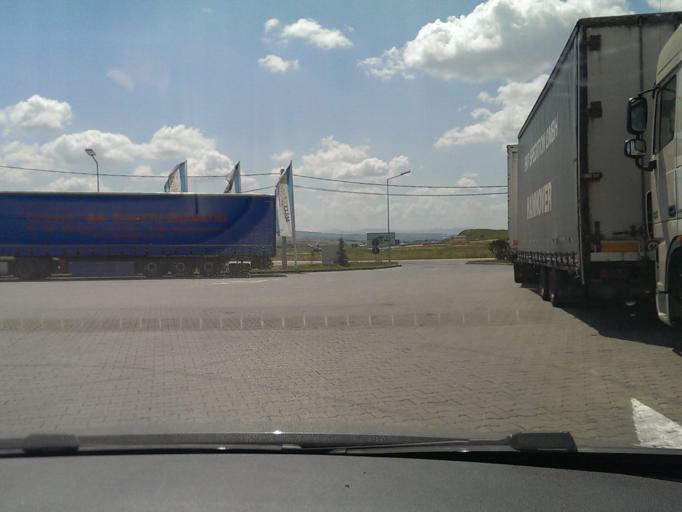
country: RO
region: Cluj
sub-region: Comuna Apahida
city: Sannicoara
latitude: 46.7983
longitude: 23.7172
